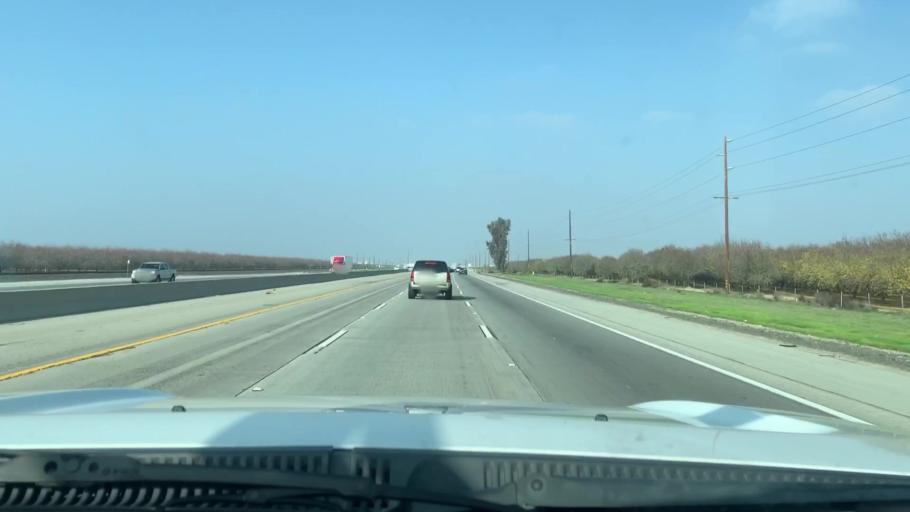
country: US
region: California
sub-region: Kern County
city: Shafter
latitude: 35.5389
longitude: -119.1934
